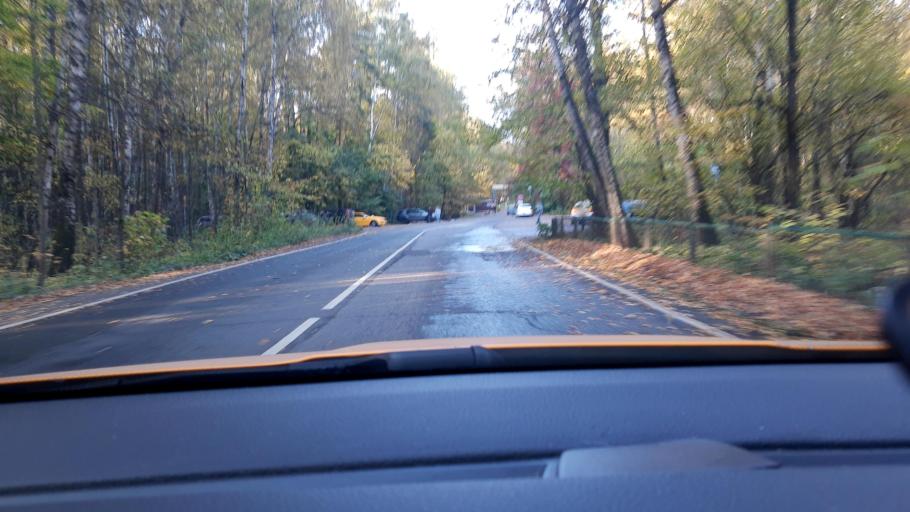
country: RU
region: Moskovskaya
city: Bogorodskoye
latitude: 55.8322
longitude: 37.7451
